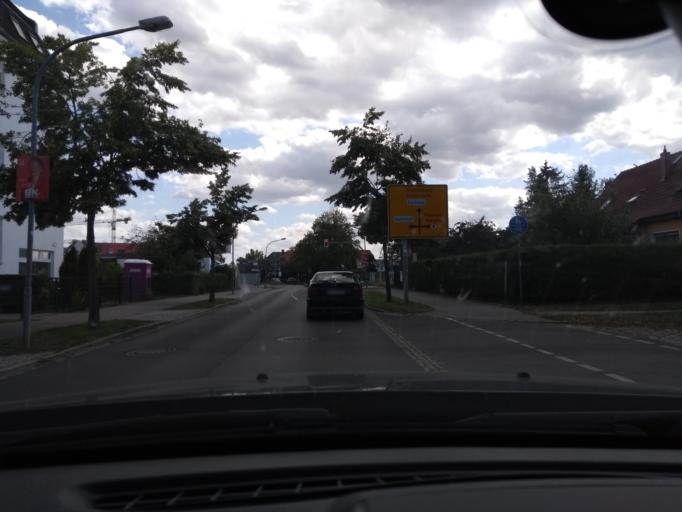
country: DE
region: Brandenburg
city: Falkensee
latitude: 52.5578
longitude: 13.0887
